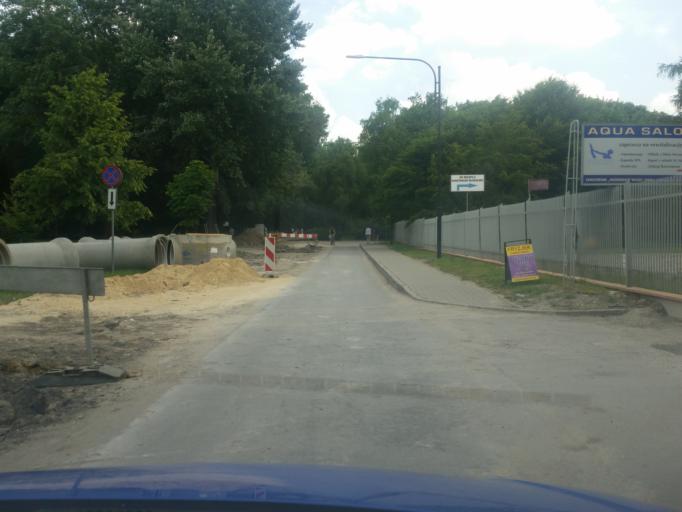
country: PL
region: Swietokrzyskie
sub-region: Powiat buski
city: Busko-Zdroj
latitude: 50.4570
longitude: 20.7164
